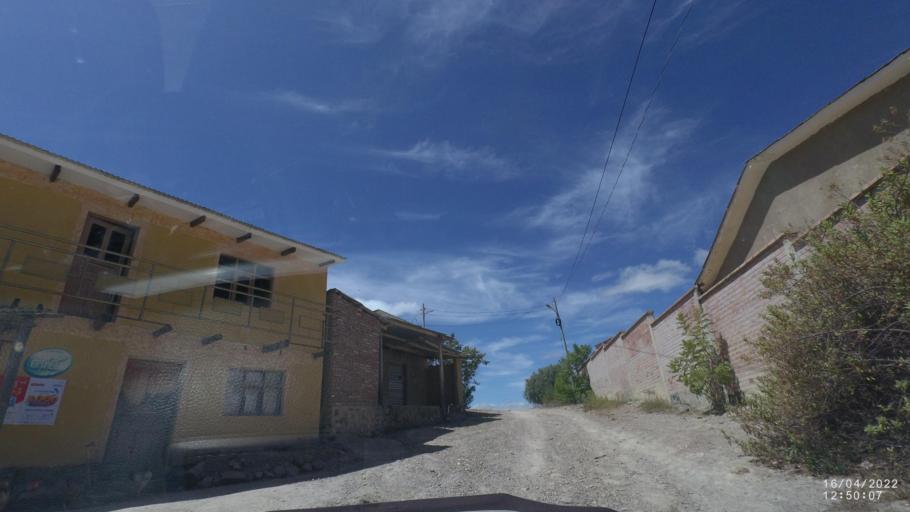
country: BO
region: Cochabamba
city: Mizque
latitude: -17.9857
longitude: -65.6284
